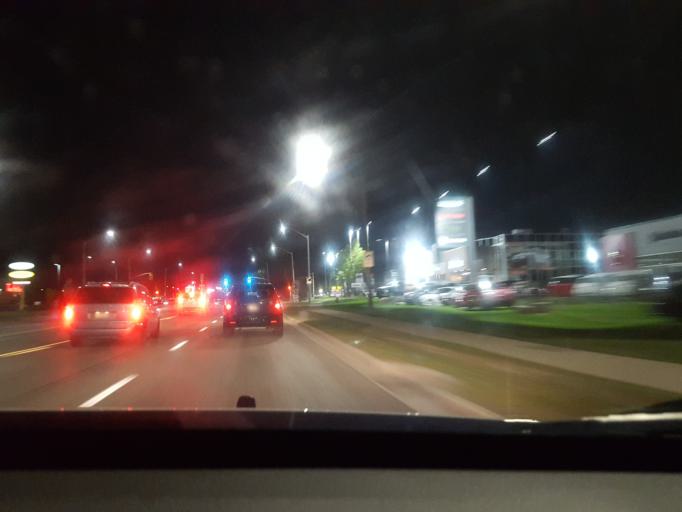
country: CA
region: Ontario
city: Hamilton
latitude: 43.2125
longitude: -79.8887
